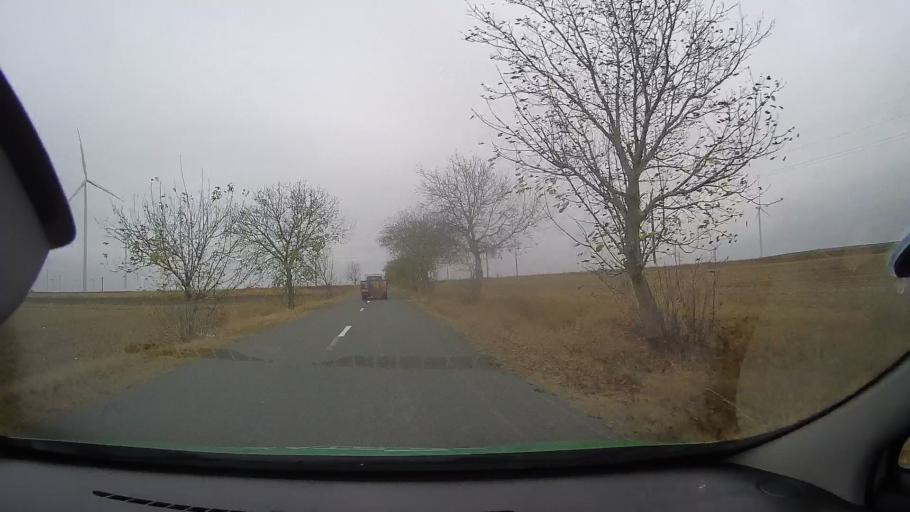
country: RO
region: Constanta
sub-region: Comuna Targusor
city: Targusor
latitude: 44.4785
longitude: 28.3763
